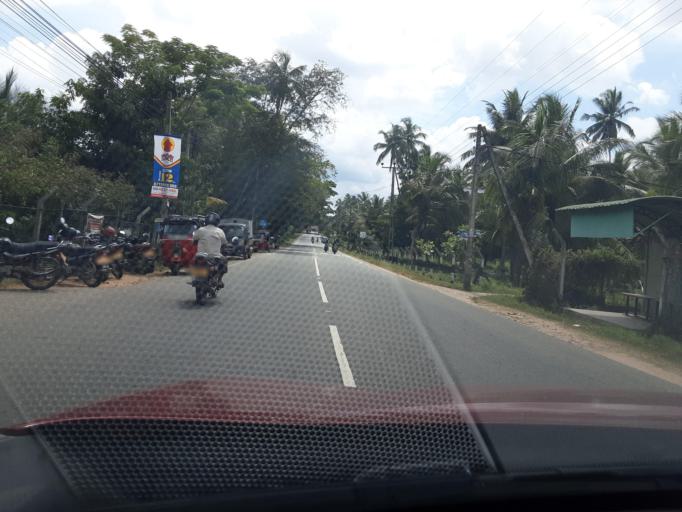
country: LK
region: North Western
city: Kuliyapitiya
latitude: 7.4521
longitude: 80.1804
